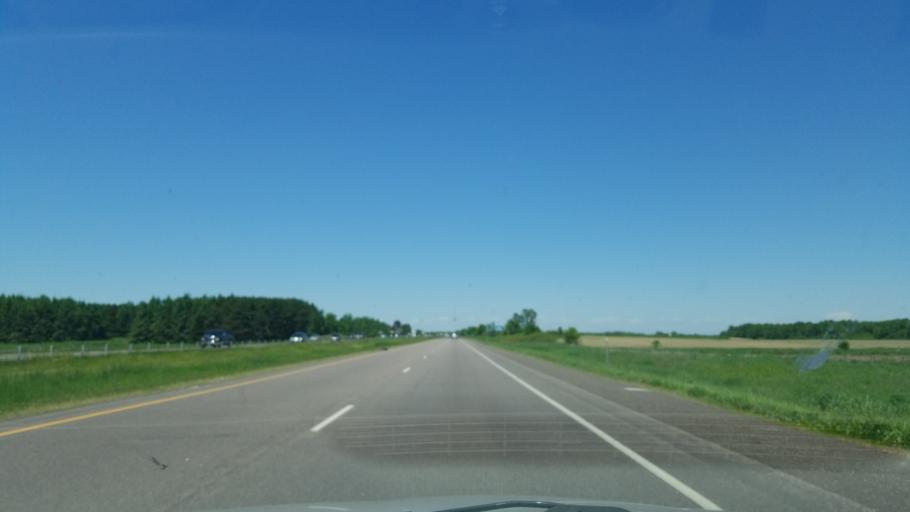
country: US
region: Minnesota
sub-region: Pine County
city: Rock Creek
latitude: 45.7246
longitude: -92.9918
